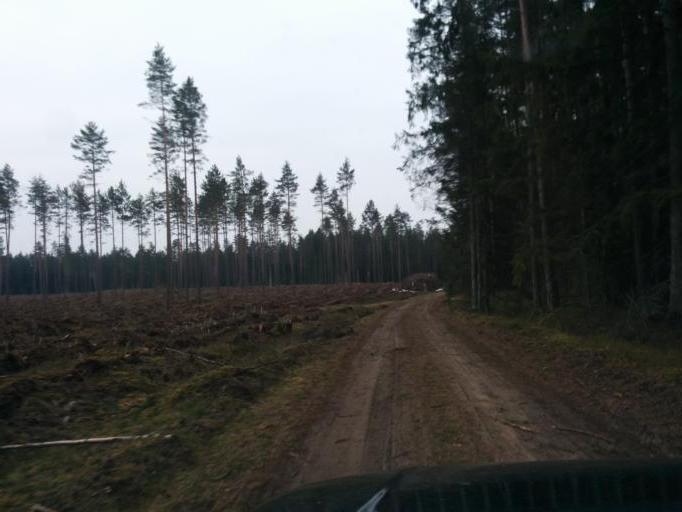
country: LV
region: Ikskile
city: Ikskile
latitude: 56.8053
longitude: 24.4831
